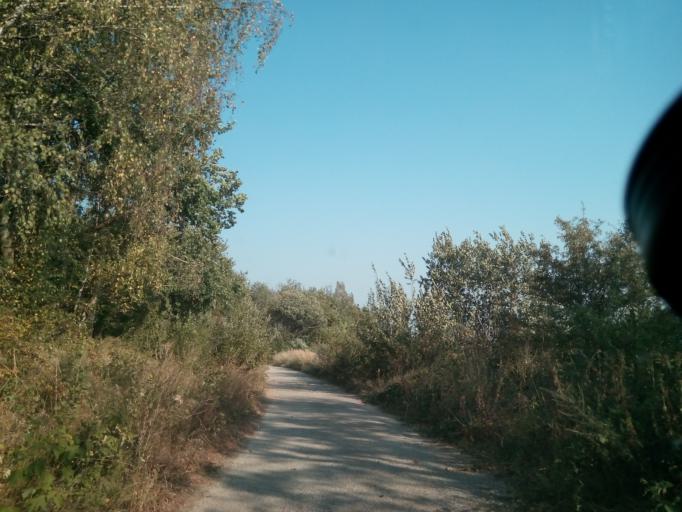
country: SK
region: Kosicky
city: Moldava nad Bodvou
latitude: 48.7337
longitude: 21.0970
